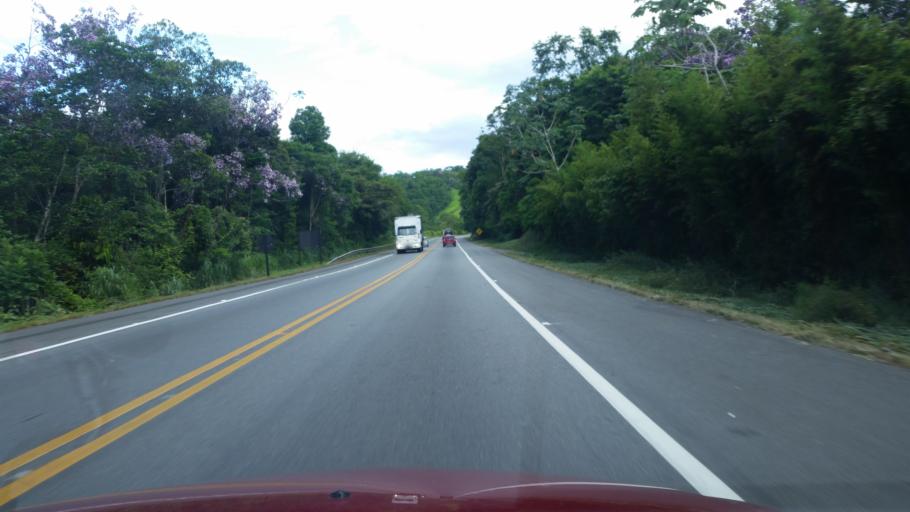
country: BR
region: Sao Paulo
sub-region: Miracatu
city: Miracatu
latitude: -24.2670
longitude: -47.2694
